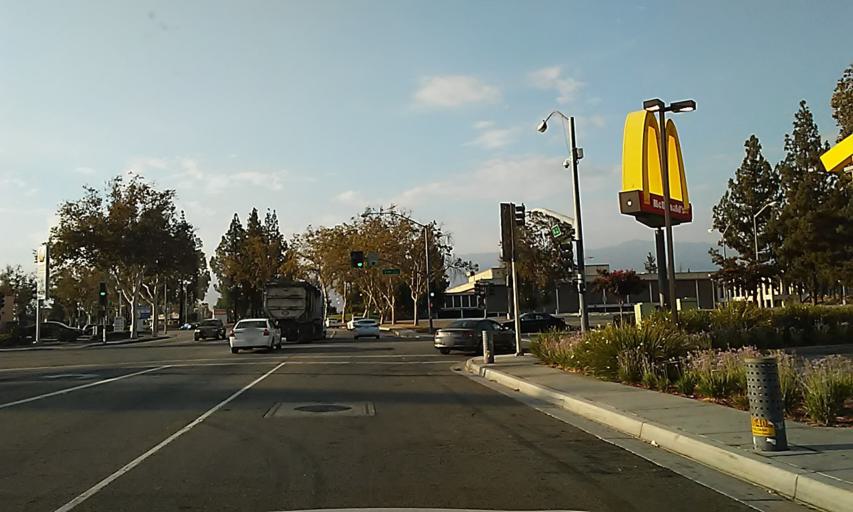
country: US
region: California
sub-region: San Bernardino County
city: San Bernardino
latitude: 34.1024
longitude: -117.2986
